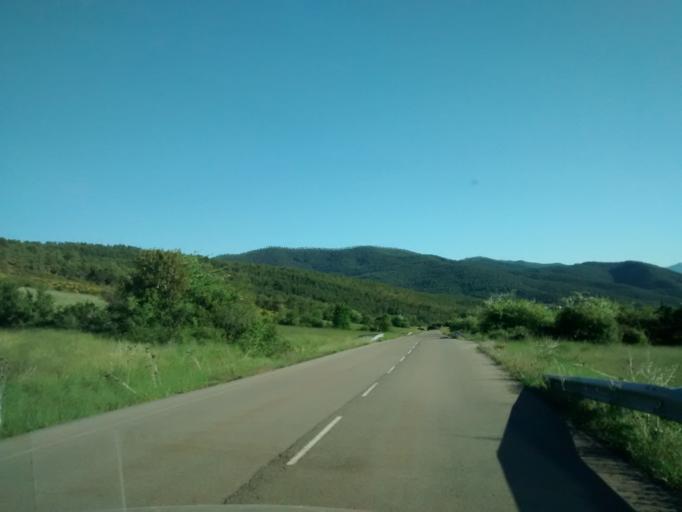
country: ES
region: Aragon
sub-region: Provincia de Huesca
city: Borau
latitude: 42.6727
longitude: -0.6208
